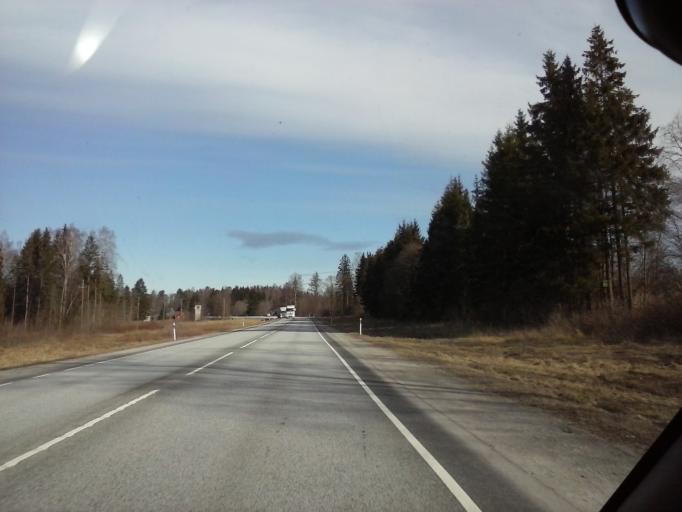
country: EE
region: Jaervamaa
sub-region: Paide linn
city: Paide
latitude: 59.0227
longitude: 25.5842
